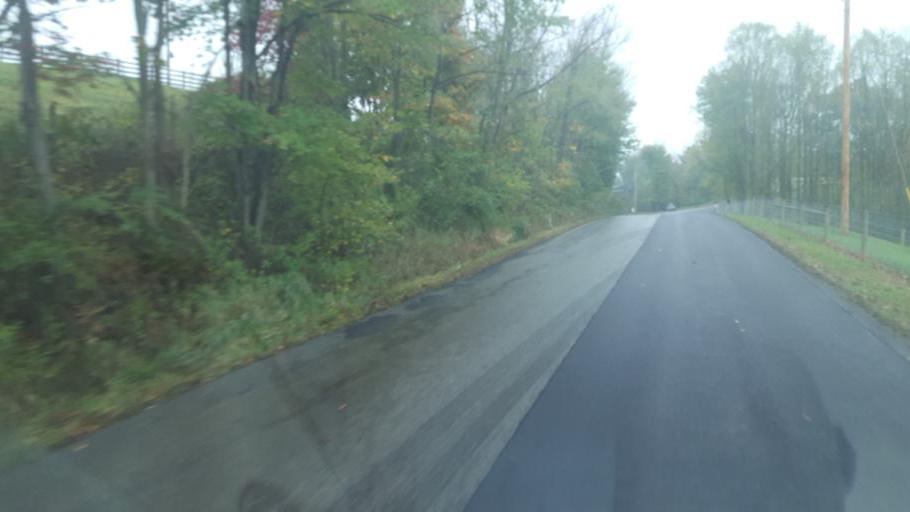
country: US
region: Ohio
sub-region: Tuscarawas County
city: Sugarcreek
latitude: 40.5754
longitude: -81.7202
